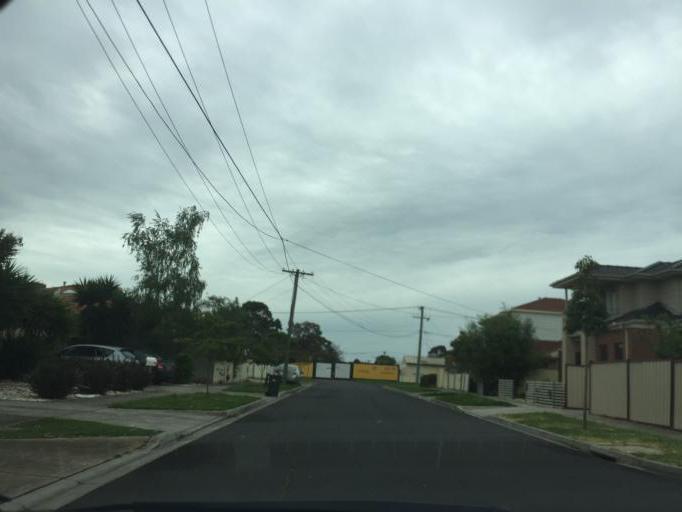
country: AU
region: Victoria
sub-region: Maribyrnong
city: Braybrook
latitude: -37.7849
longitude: 144.8393
